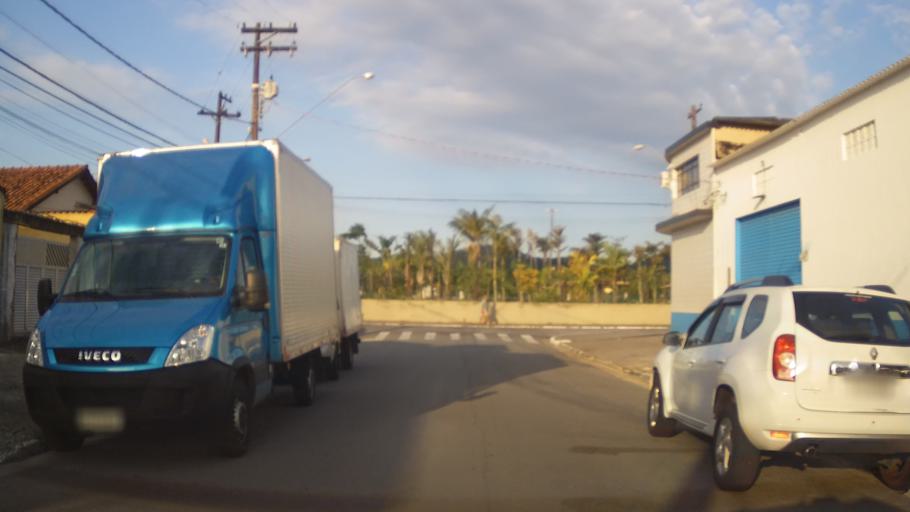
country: BR
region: Sao Paulo
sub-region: Praia Grande
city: Praia Grande
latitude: -23.9969
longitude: -46.4165
